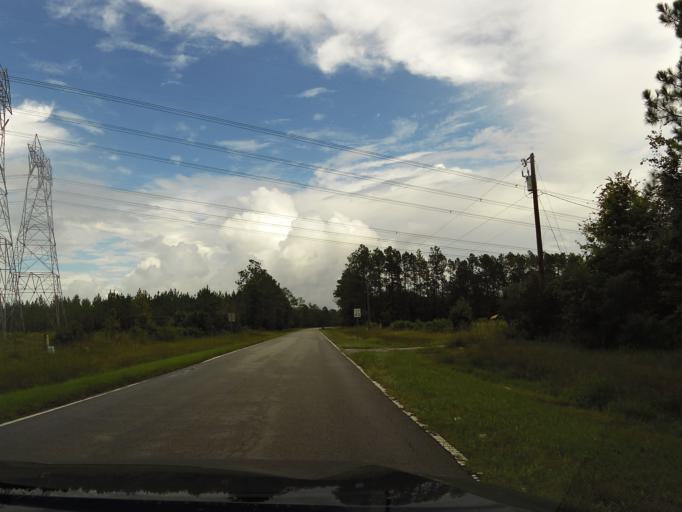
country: US
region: Florida
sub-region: Duval County
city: Baldwin
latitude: 30.3964
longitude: -81.9514
